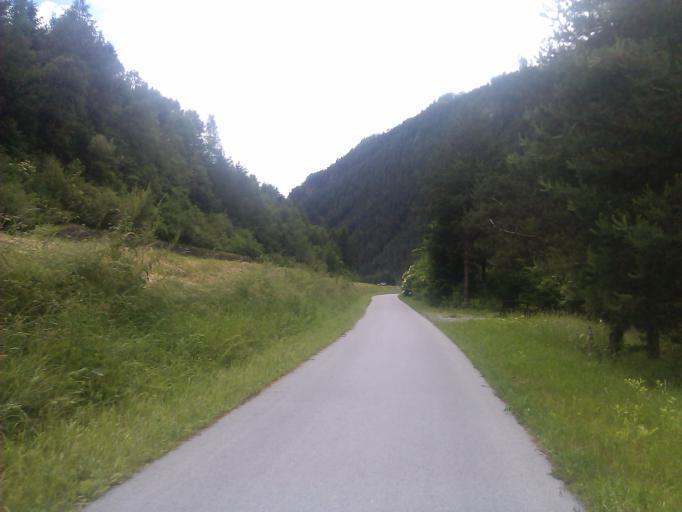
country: AT
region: Tyrol
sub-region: Politischer Bezirk Landeck
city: Ried im Oberinntal
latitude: 47.0431
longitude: 10.6363
